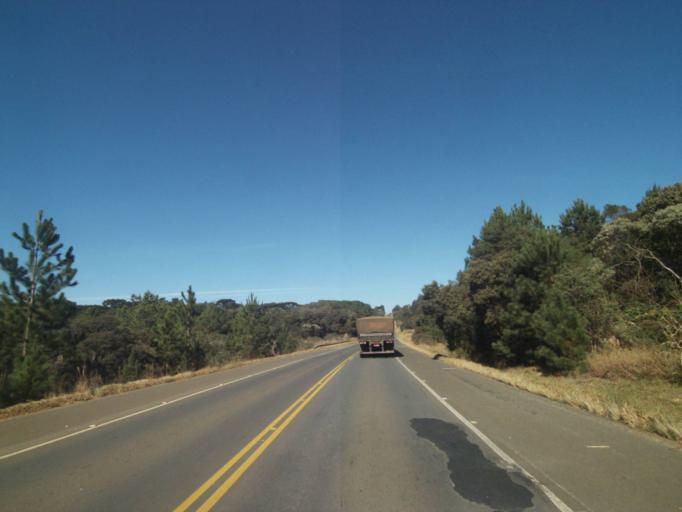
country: BR
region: Parana
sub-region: Tibagi
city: Tibagi
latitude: -24.5872
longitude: -50.4368
